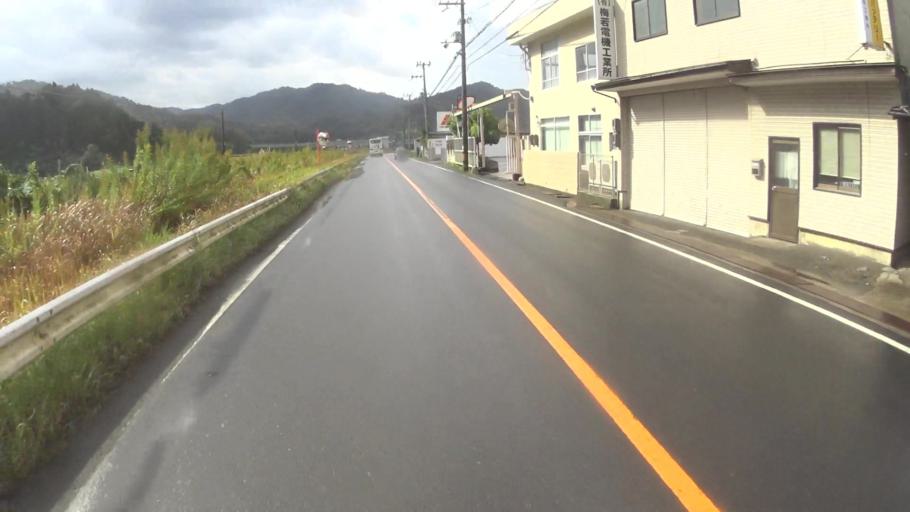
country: JP
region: Kyoto
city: Miyazu
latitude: 35.5569
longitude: 135.1635
